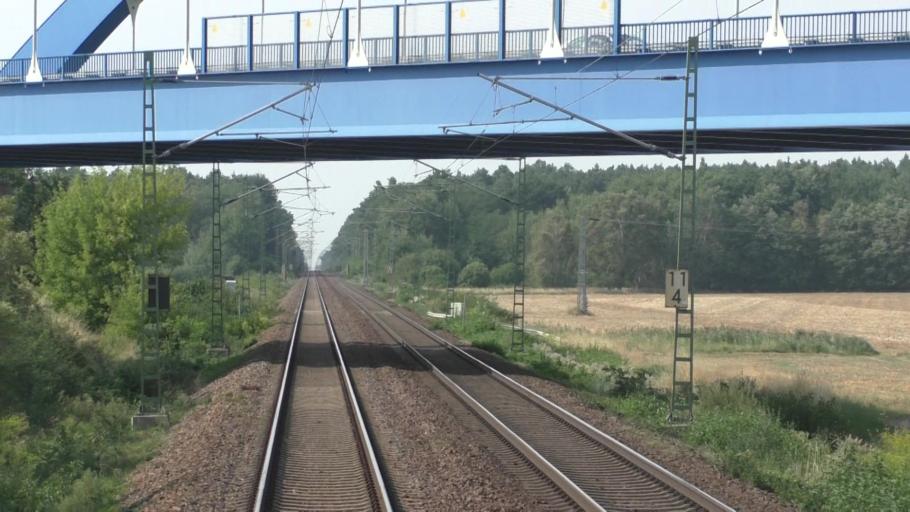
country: DE
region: Saxony-Anhalt
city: Gommern
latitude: 52.0854
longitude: 11.8205
